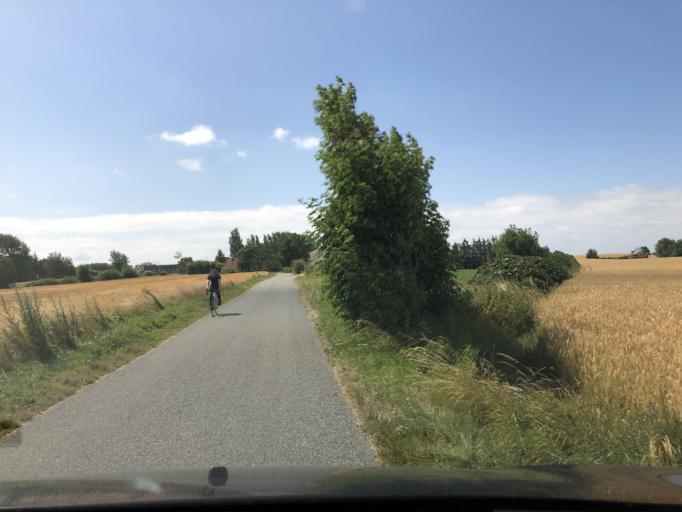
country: DK
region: South Denmark
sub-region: AEro Kommune
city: AEroskobing
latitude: 54.9347
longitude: 10.2824
